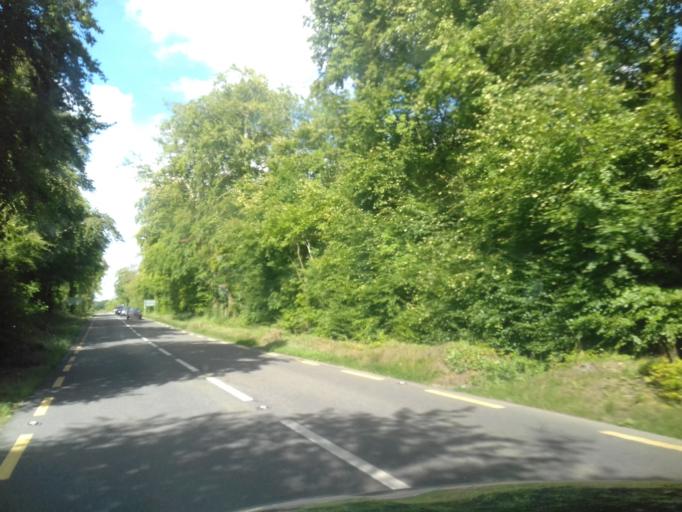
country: IE
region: Leinster
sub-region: Wicklow
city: Blessington
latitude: 53.1425
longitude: -6.5598
